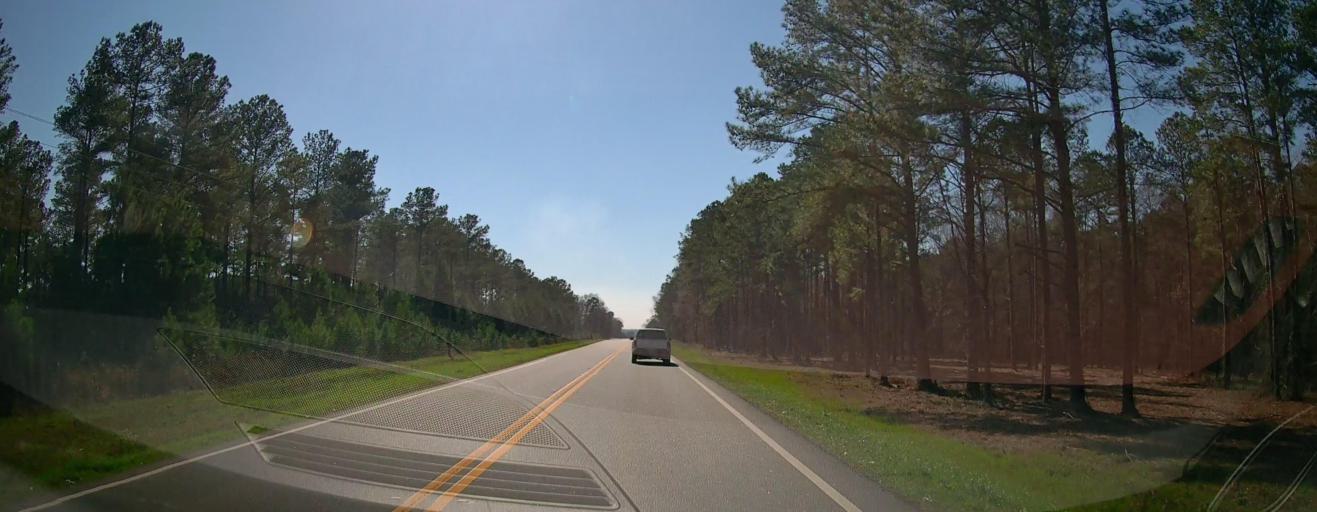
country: US
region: Georgia
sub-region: Dooly County
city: Unadilla
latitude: 32.3346
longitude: -83.8592
